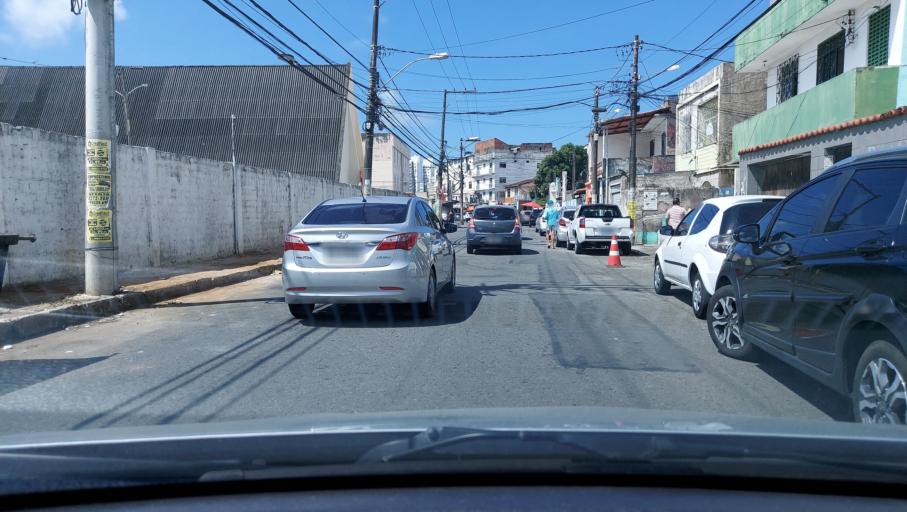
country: BR
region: Bahia
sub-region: Salvador
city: Salvador
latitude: -12.9867
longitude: -38.4785
